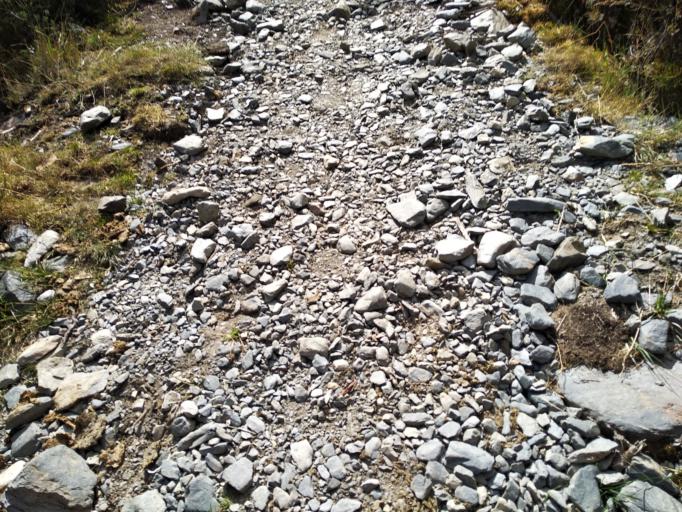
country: PE
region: Cusco
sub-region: Provincia de Urubamba
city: Ollantaytambo
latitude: -13.1272
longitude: -72.3346
